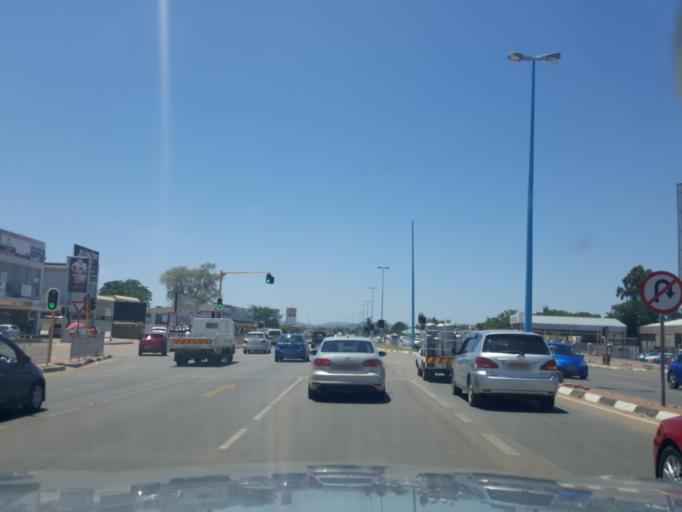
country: BW
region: Kweneng
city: Mogoditshane
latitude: -24.6291
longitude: 25.8720
